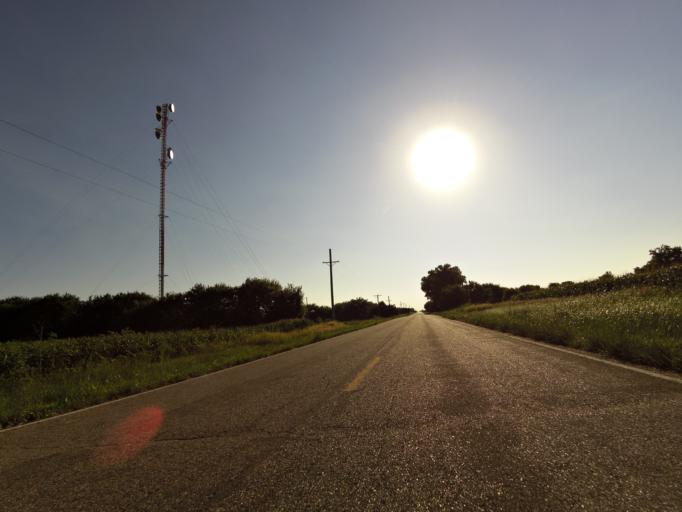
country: US
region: Kansas
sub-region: McPherson County
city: Moundridge
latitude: 38.1451
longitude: -97.5827
